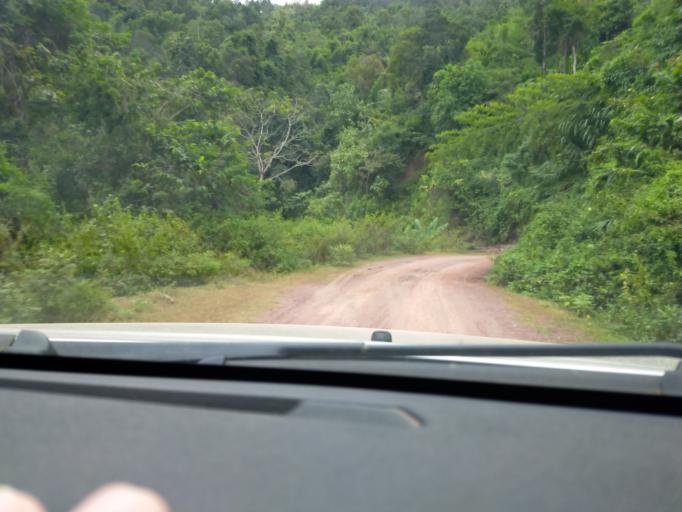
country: TH
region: Nan
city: Chaloem Phra Kiat
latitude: 19.7846
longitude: 101.3617
